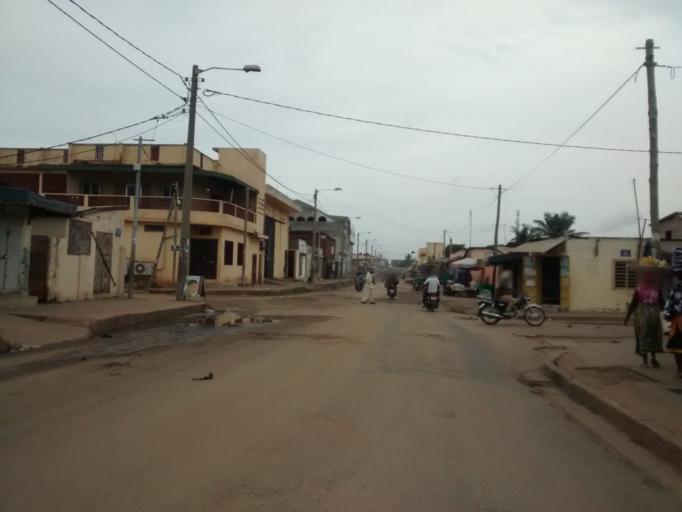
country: TG
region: Maritime
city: Lome
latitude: 6.1447
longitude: 1.2164
